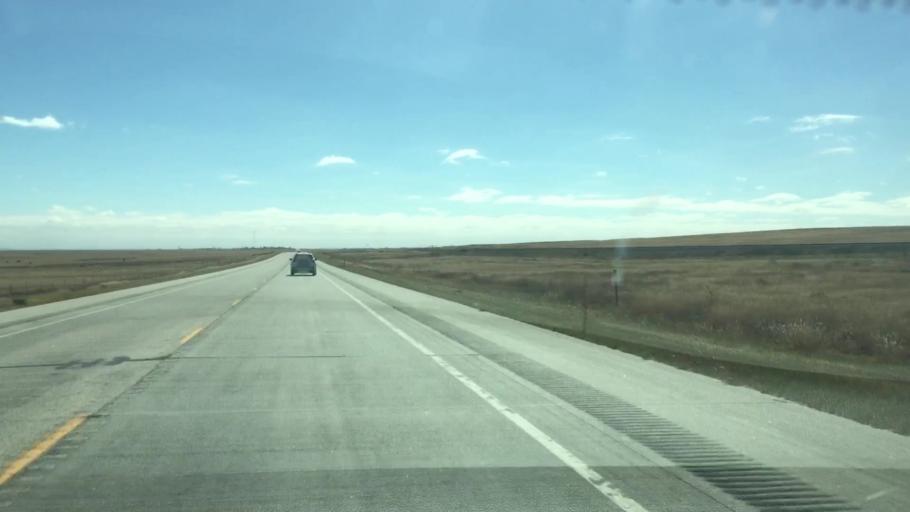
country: US
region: Colorado
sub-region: Lincoln County
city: Hugo
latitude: 39.1729
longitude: -103.5351
